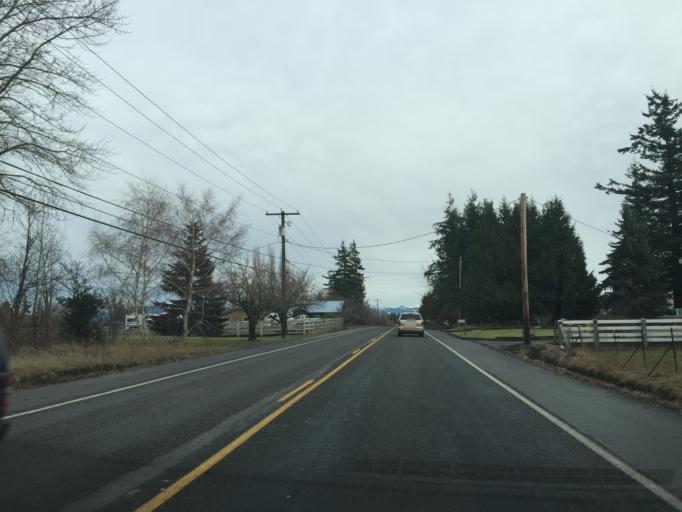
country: US
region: Washington
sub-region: Whatcom County
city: Marietta-Alderwood
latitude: 48.8169
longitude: -122.5346
